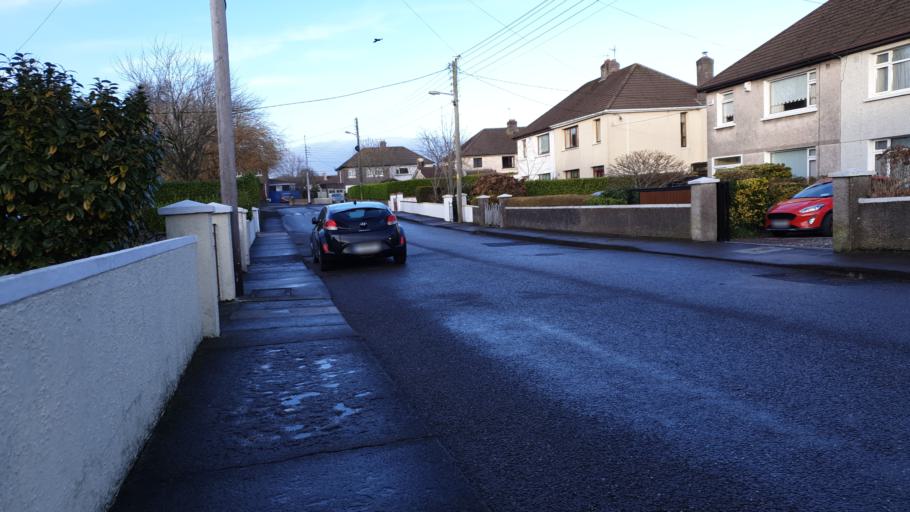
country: IE
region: Munster
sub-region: County Cork
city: Cork
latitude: 51.8905
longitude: -8.4241
